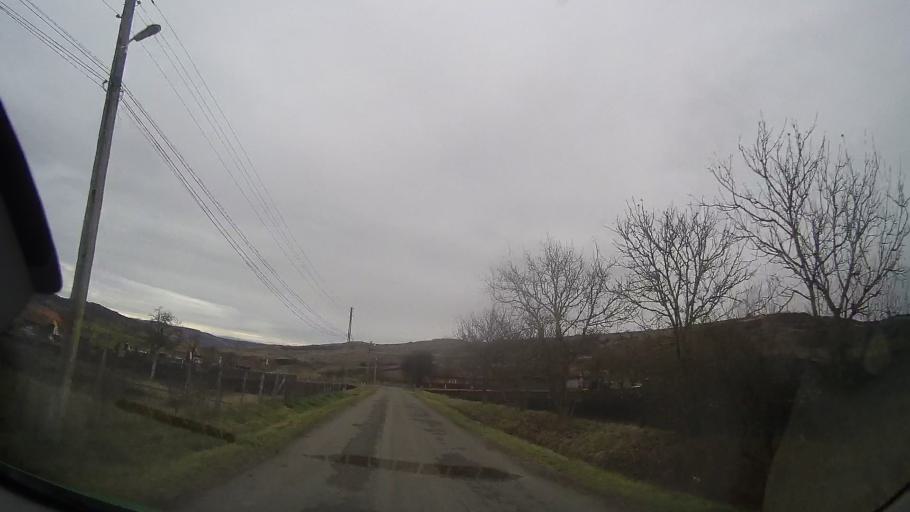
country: RO
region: Mures
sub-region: Comuna Bala
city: Bala
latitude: 46.7059
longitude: 24.5005
